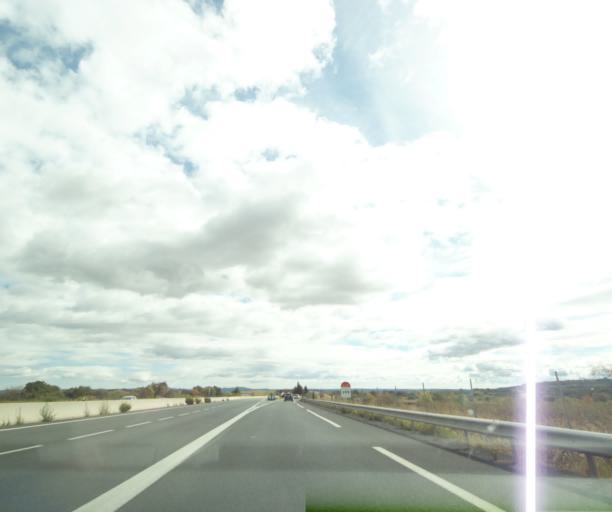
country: FR
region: Languedoc-Roussillon
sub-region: Departement de l'Herault
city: Nebian
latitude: 43.6584
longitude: 3.4440
